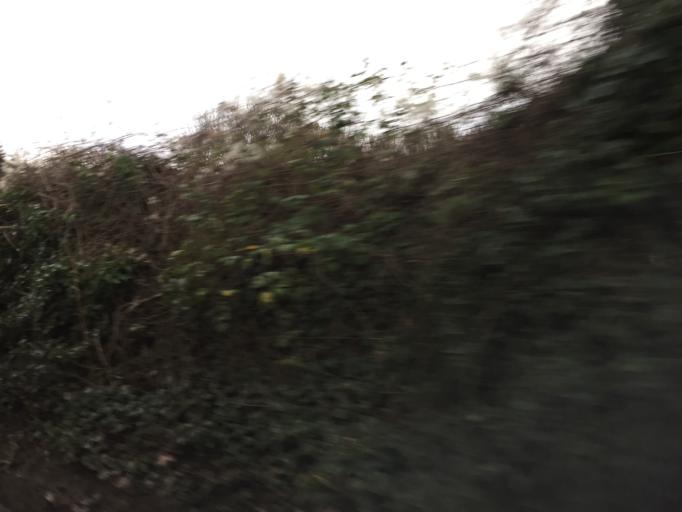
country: GB
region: Wales
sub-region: Monmouthshire
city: Rogiet
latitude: 51.6024
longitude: -2.7825
